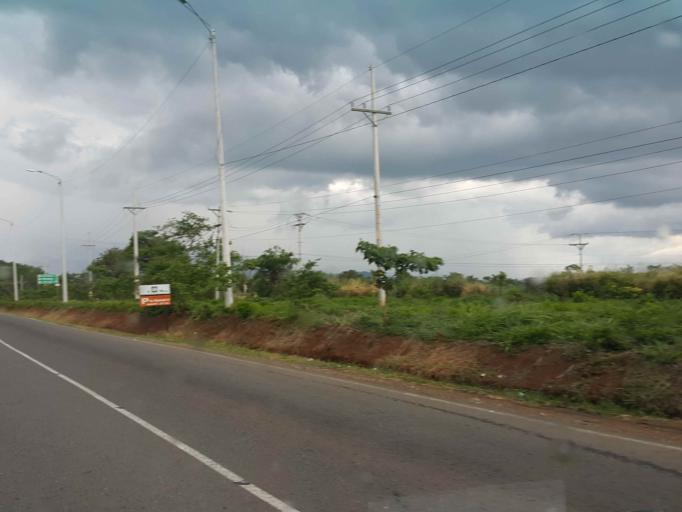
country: CR
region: Puntarenas
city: Miramar
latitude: 10.0941
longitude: -84.8207
